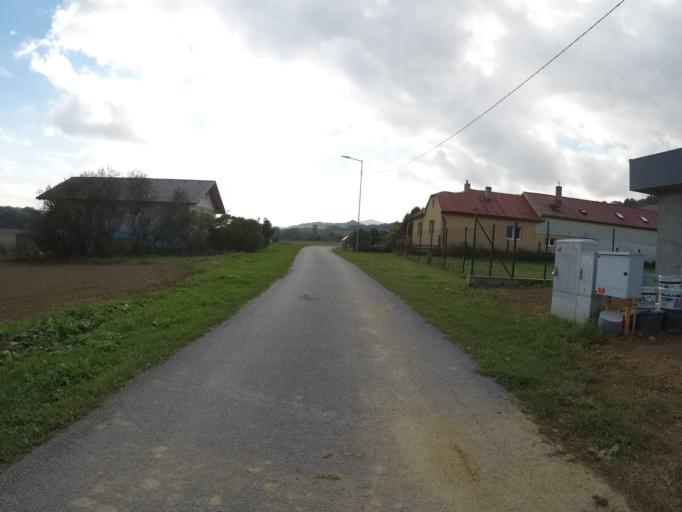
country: SK
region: Presovsky
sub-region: Okres Presov
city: Presov
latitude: 48.9355
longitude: 21.1800
